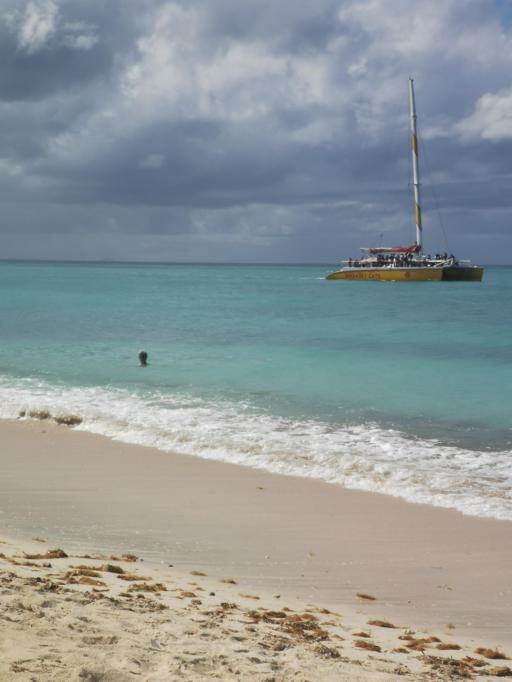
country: AG
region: Saint John
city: Saint John's
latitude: 17.1245
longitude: -61.8799
